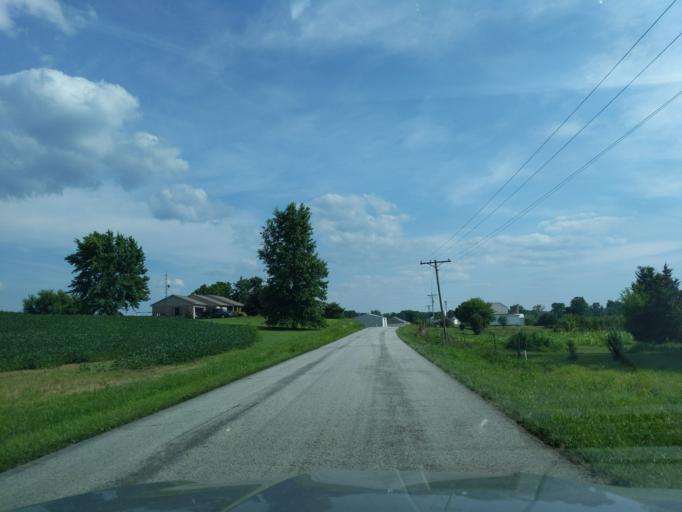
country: US
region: Indiana
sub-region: Decatur County
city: Greensburg
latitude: 39.2648
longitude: -85.4651
